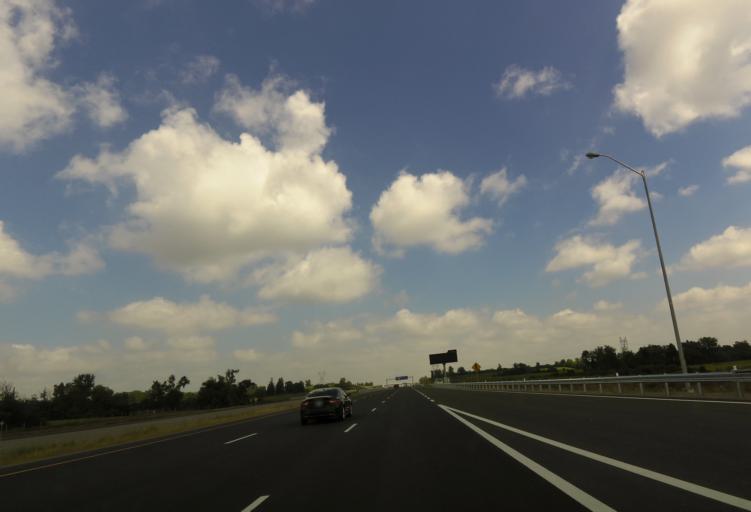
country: CA
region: Ontario
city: Ajax
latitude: 43.9434
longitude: -79.0471
